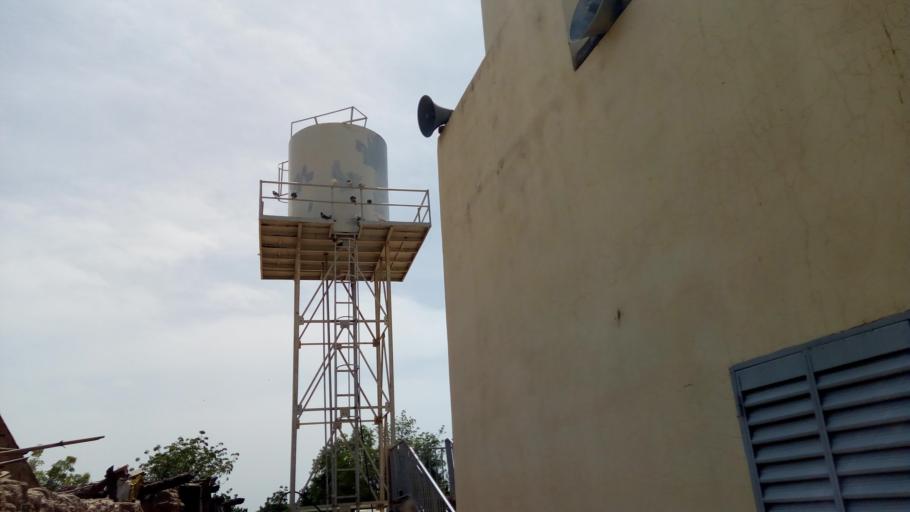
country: ML
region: Kayes
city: Kita
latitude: 13.4002
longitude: -8.8607
